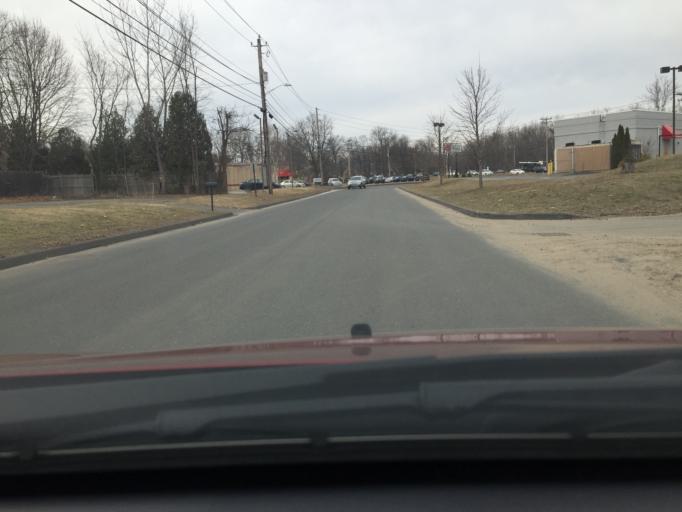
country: US
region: Massachusetts
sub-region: Hampden County
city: Westfield
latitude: 42.1142
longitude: -72.7323
